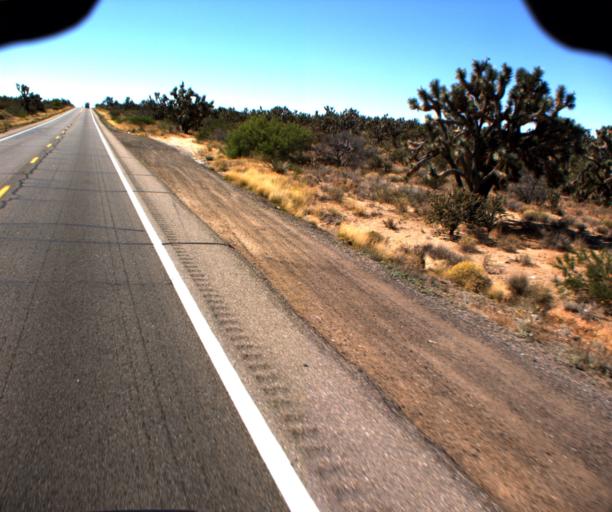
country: US
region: Arizona
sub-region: Yavapai County
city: Congress
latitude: 34.2602
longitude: -113.0879
